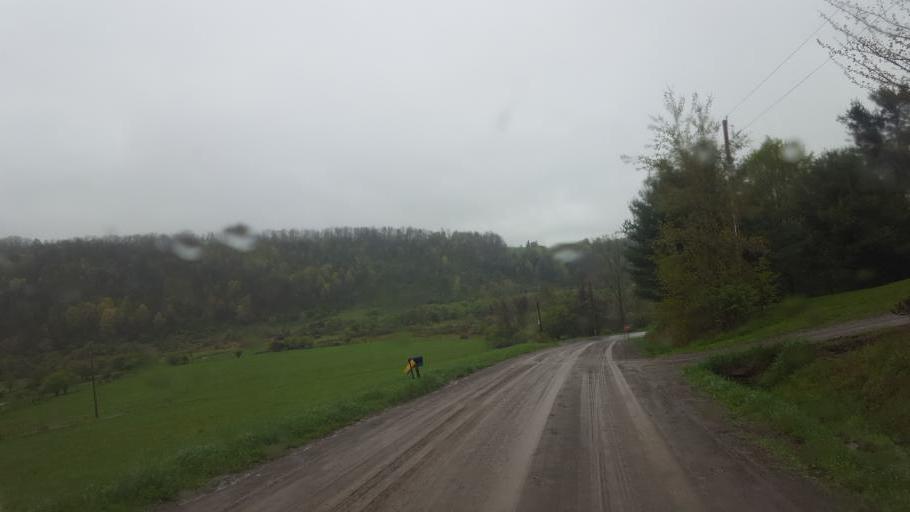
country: US
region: Pennsylvania
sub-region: Tioga County
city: Elkland
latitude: 42.0657
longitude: -77.4350
